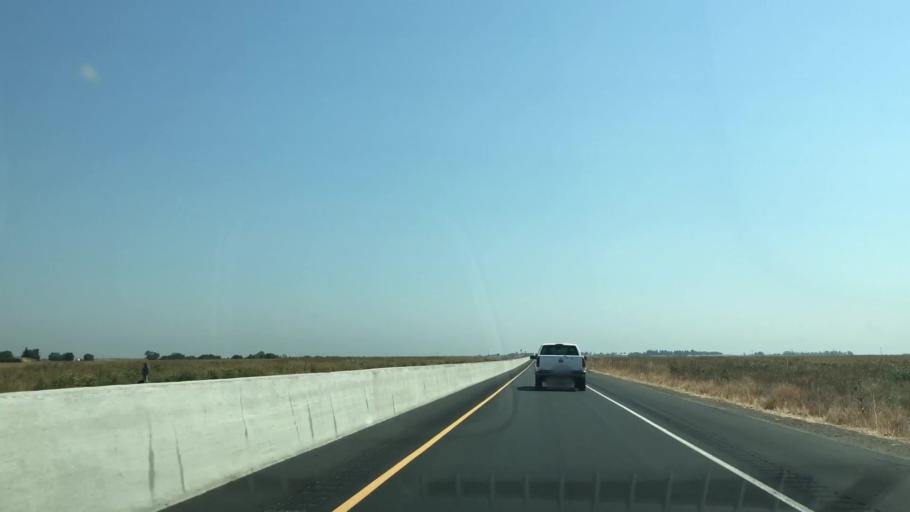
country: US
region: California
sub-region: Sacramento County
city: Walnut Grove
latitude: 38.1131
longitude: -121.5434
